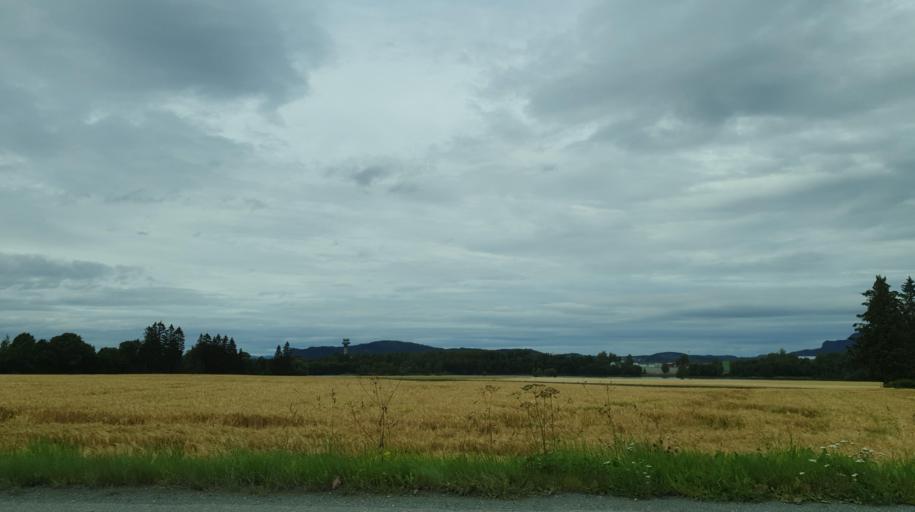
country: NO
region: Nord-Trondelag
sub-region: Stjordal
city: Stjordalshalsen
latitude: 63.4462
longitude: 10.9418
